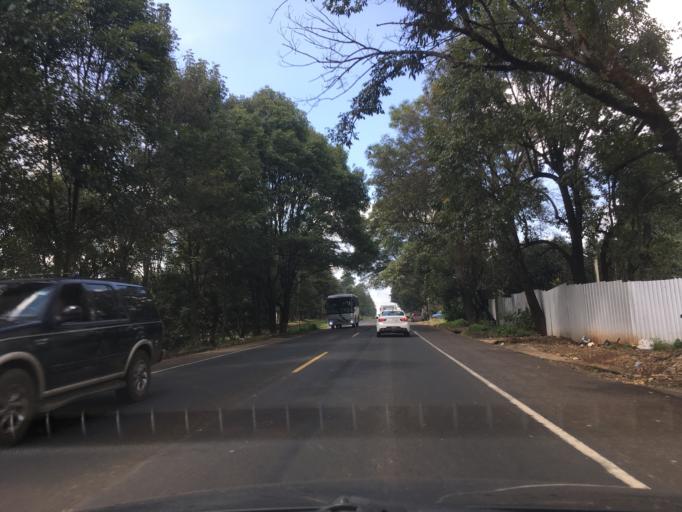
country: MX
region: Michoacan
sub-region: Tingueindin
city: Tingueindin
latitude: 19.7547
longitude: -102.4894
